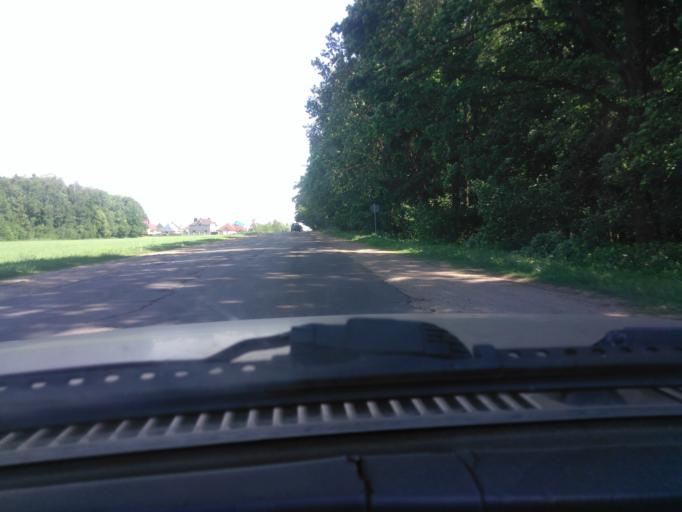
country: BY
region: Mogilev
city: Palykavichy Pyershyya
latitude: 53.9548
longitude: 30.3669
